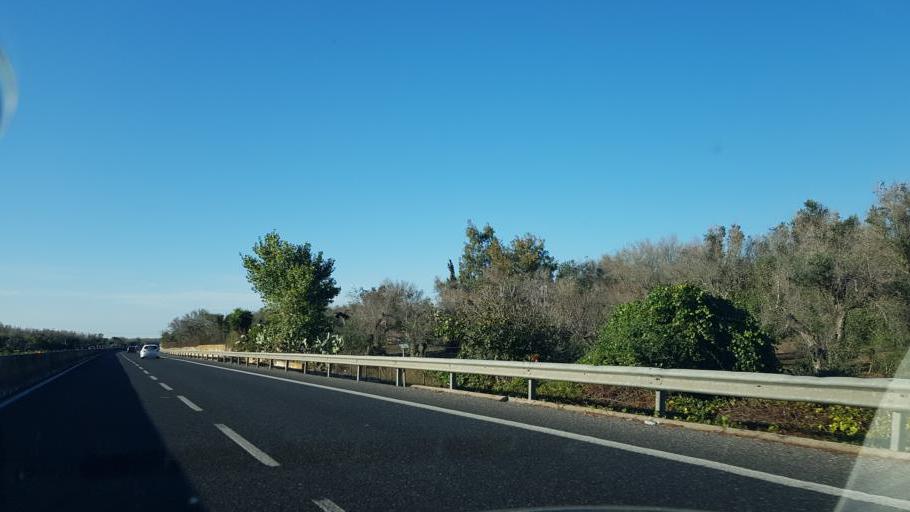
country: IT
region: Apulia
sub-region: Provincia di Brindisi
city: Torchiarolo
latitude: 40.4660
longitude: 18.0548
